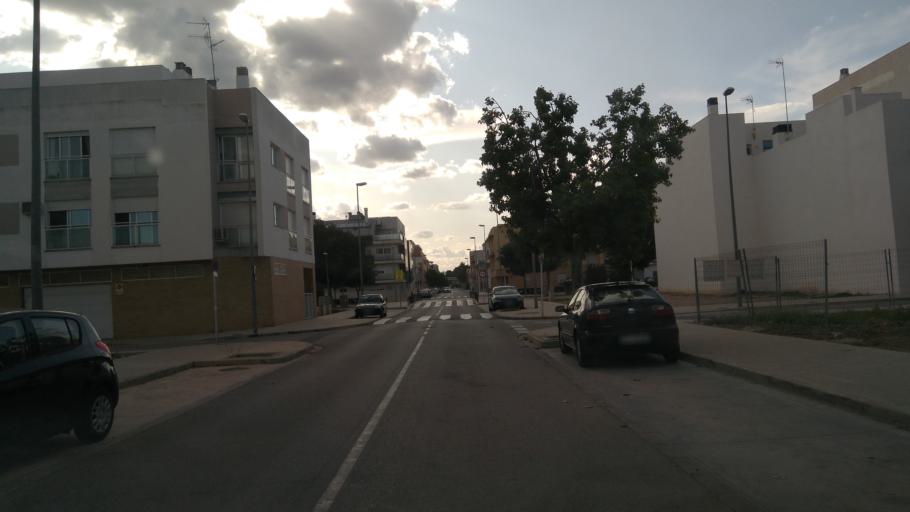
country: ES
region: Valencia
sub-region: Provincia de Valencia
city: L'Alcudia
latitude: 39.1932
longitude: -0.5001
